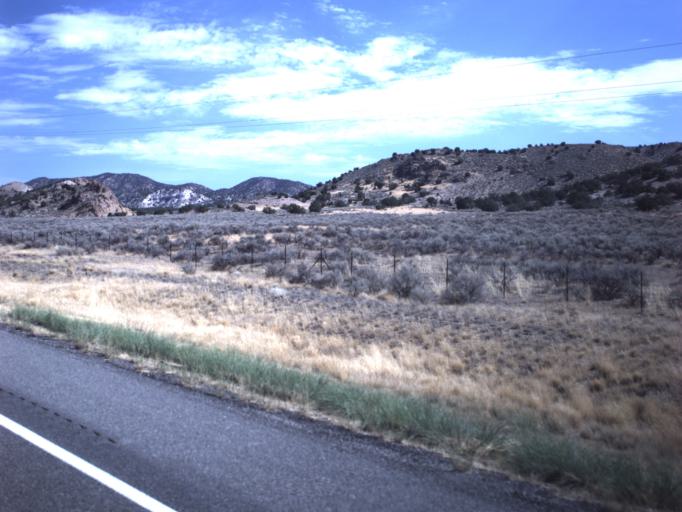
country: US
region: Utah
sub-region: Sanpete County
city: Gunnison
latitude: 39.3589
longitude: -111.9297
